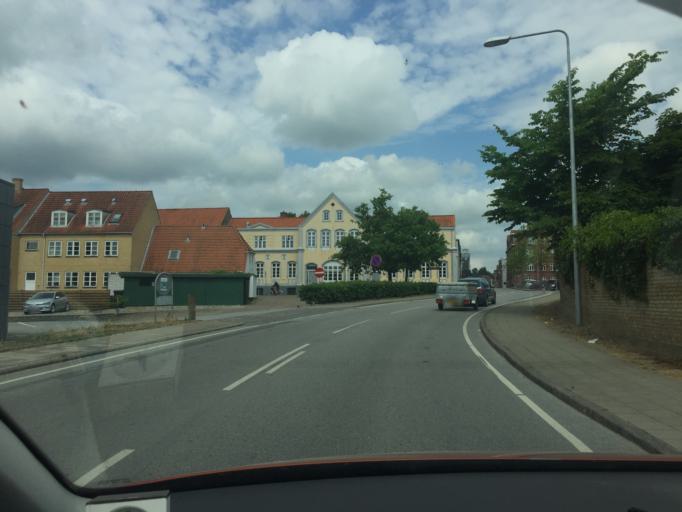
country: DK
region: South Denmark
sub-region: Haderslev Kommune
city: Haderslev
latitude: 55.2487
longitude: 9.4943
